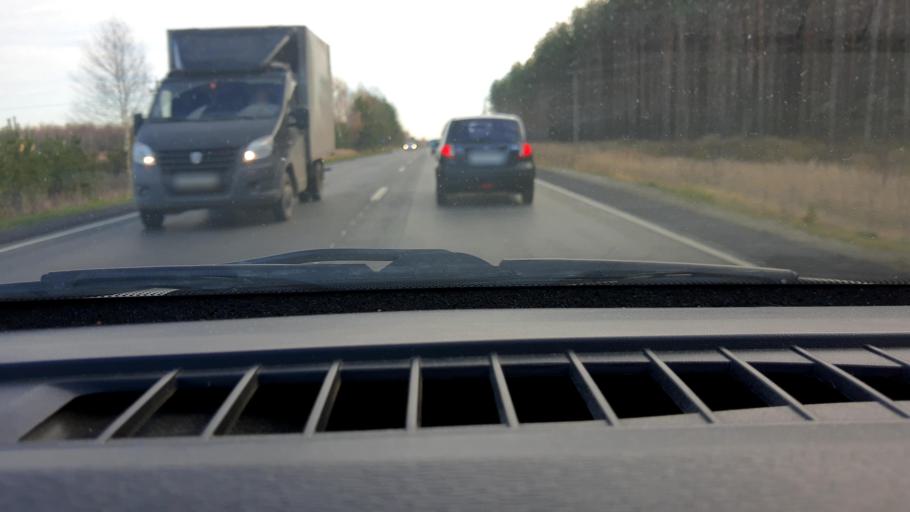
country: RU
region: Nizjnij Novgorod
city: Novaya Balakhna
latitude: 56.6079
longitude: 43.6124
